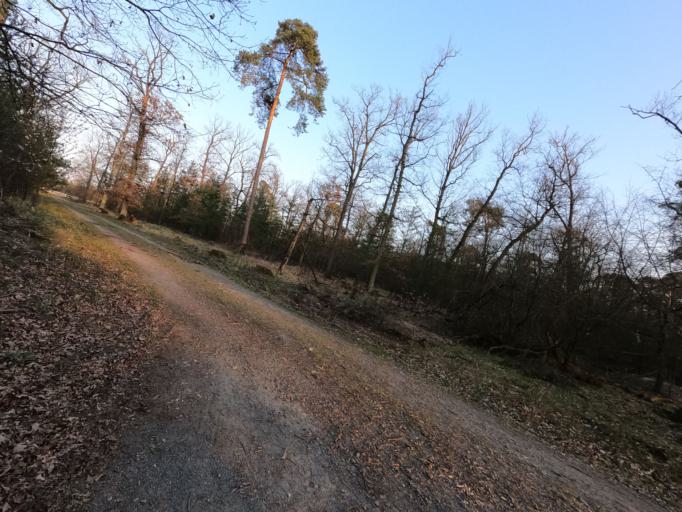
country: DE
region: Hesse
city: Kelsterbach
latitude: 50.0183
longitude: 8.5201
